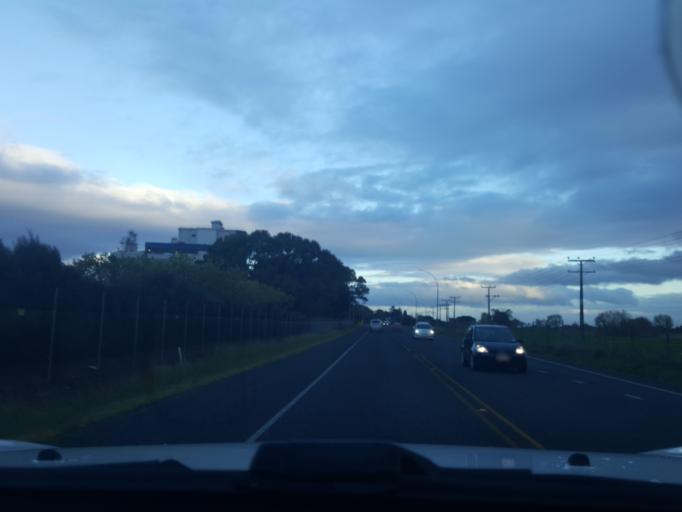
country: NZ
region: Waikato
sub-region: Waikato District
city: Ngaruawahia
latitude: -37.7160
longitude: 175.2120
